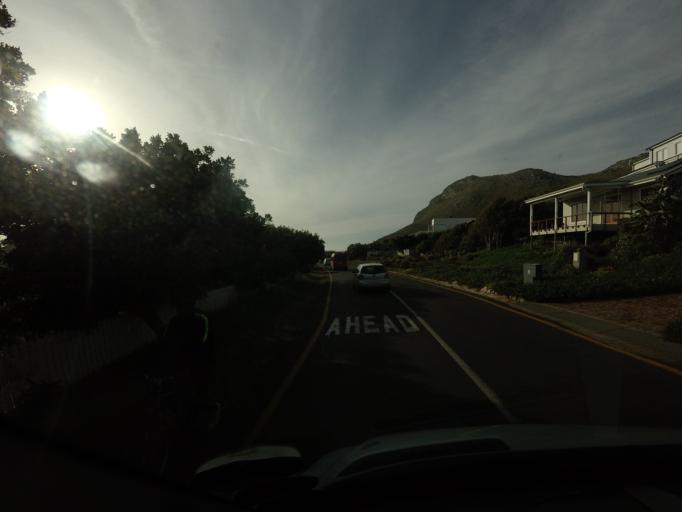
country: ZA
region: Western Cape
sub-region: City of Cape Town
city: Bergvliet
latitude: -34.1986
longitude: 18.3764
